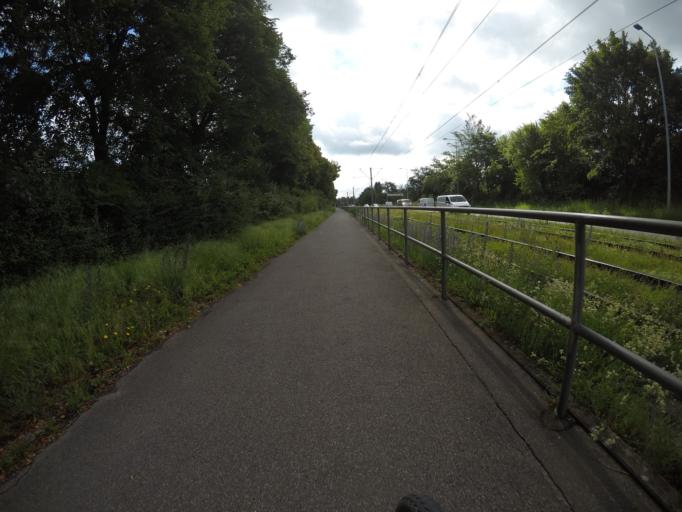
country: DE
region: Baden-Wuerttemberg
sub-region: Regierungsbezirk Stuttgart
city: Ostfildern
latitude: 48.7404
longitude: 9.2222
